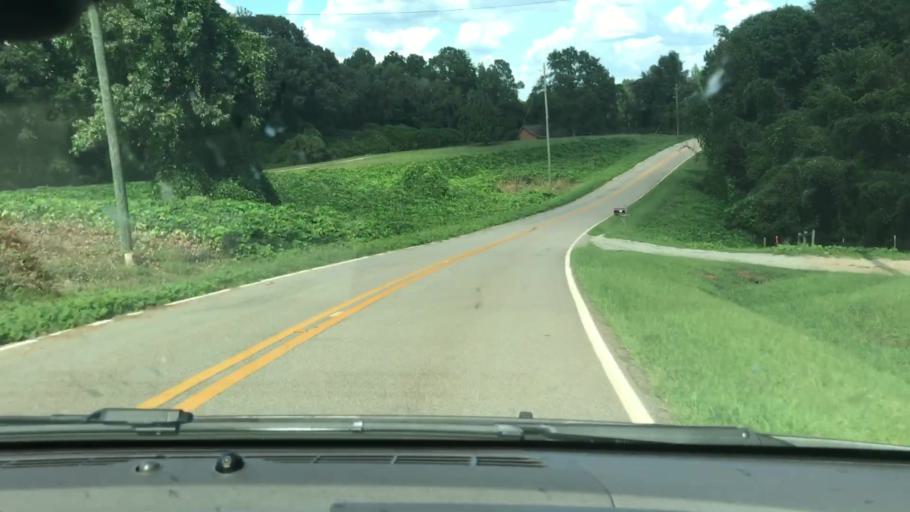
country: US
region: Georgia
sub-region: Troup County
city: La Grange
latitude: 33.1294
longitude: -85.1271
